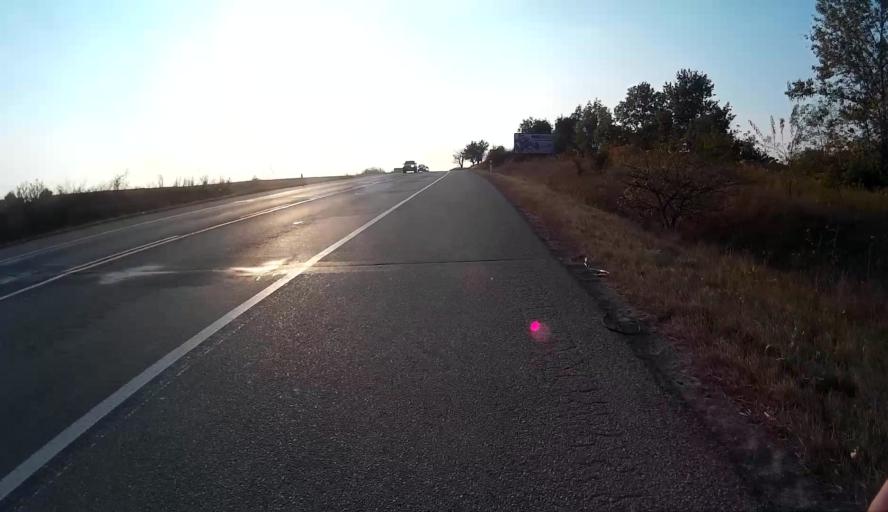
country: CZ
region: South Moravian
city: Podoli
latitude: 49.1826
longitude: 16.7114
